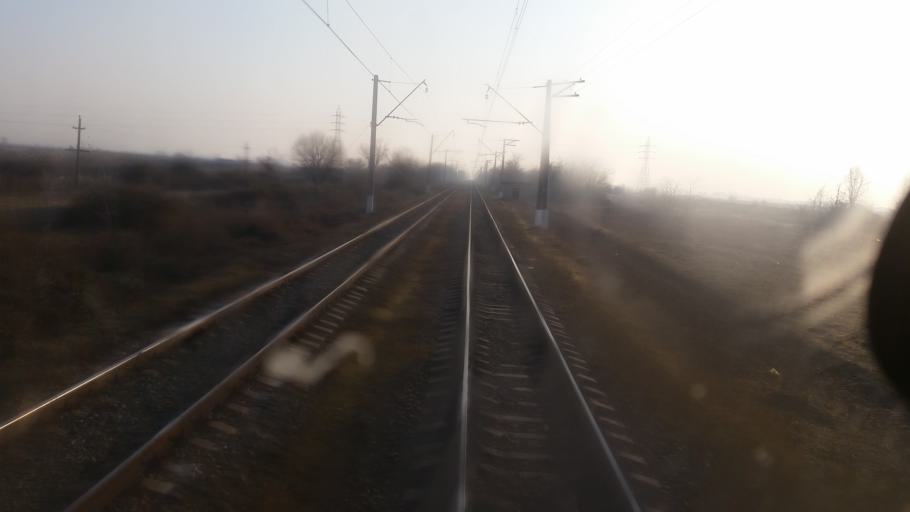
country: AZ
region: Yevlax City
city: Yevlakh
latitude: 40.6300
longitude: 47.0650
